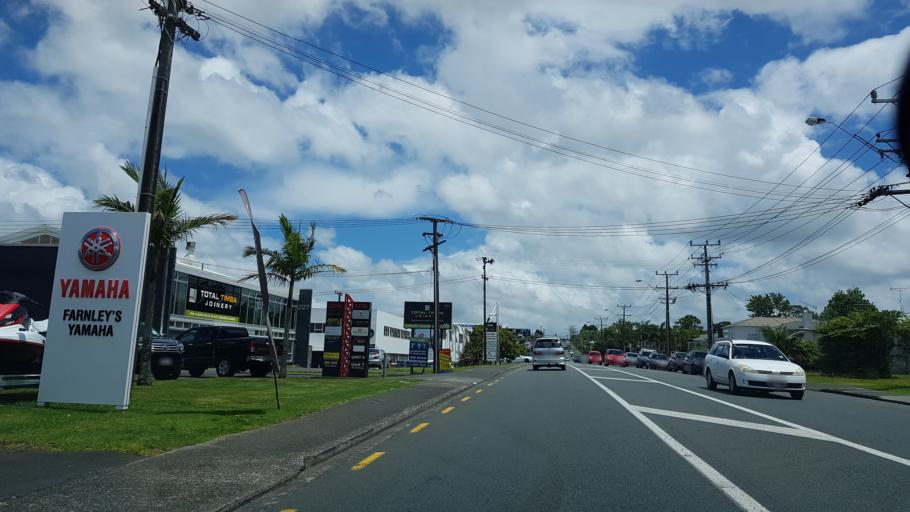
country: NZ
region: Auckland
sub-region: Auckland
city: North Shore
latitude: -36.7790
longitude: 174.7417
